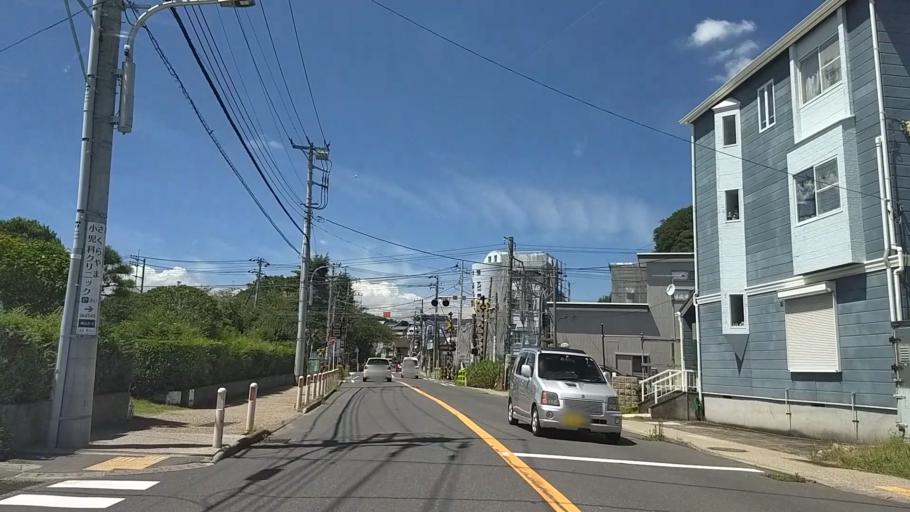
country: JP
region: Kanagawa
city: Zushi
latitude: 35.2990
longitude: 139.5946
